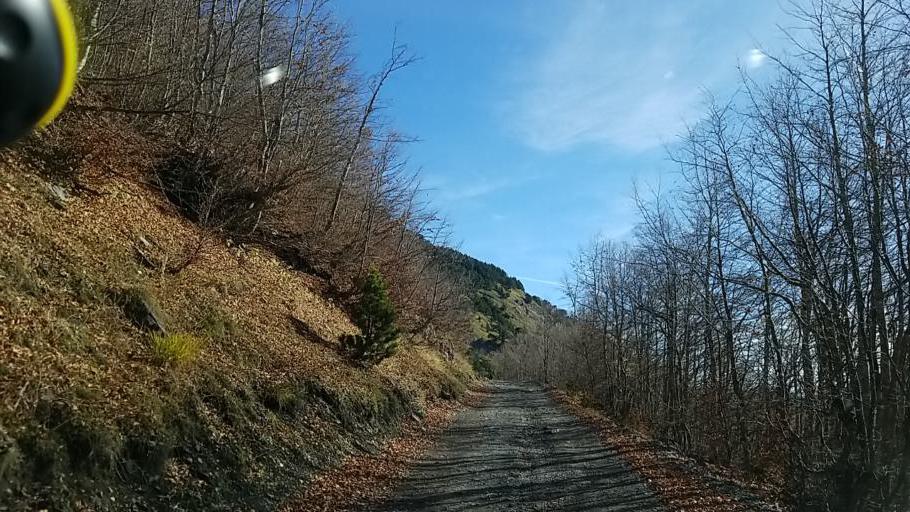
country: AL
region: Shkoder
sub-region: Rrethi i Shkodres
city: Nicaj-Shale
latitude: 42.3893
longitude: 19.7218
